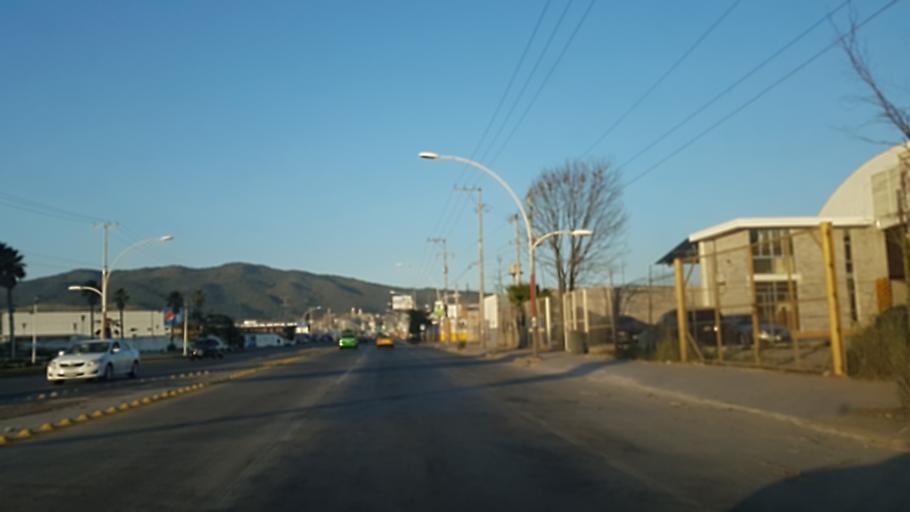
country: MX
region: Nayarit
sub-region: Tepic
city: La Corregidora
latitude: 21.4758
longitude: -104.8474
